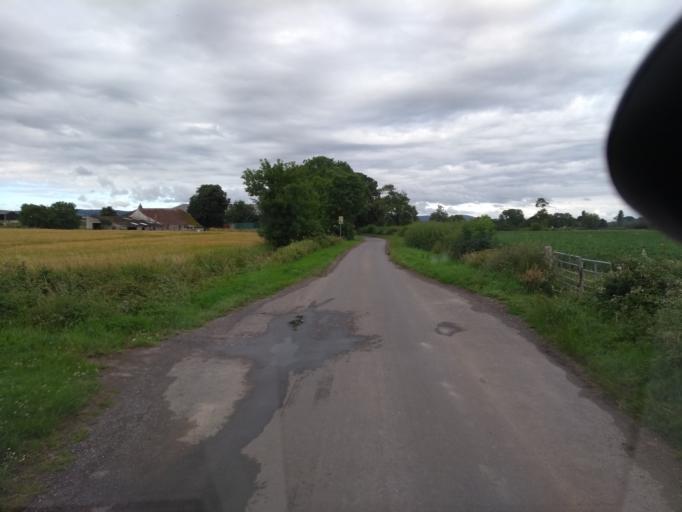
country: GB
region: England
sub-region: Somerset
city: Bridgwater
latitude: 51.1469
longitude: -3.0126
